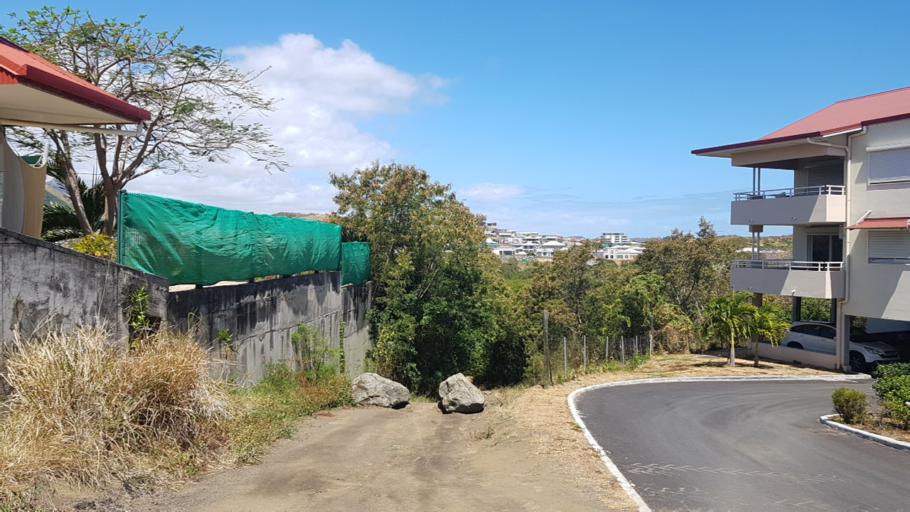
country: NC
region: South Province
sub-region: Dumbea
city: Dumbea
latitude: -22.1982
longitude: 166.4367
